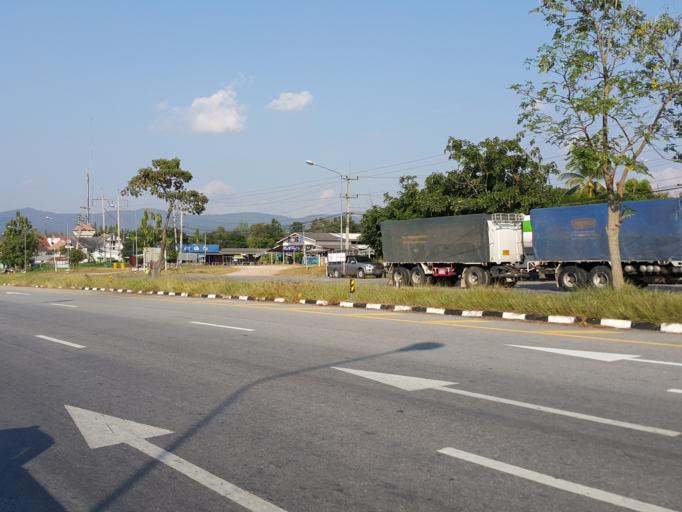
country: TH
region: Lampang
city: Thoen
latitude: 17.6283
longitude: 99.2381
